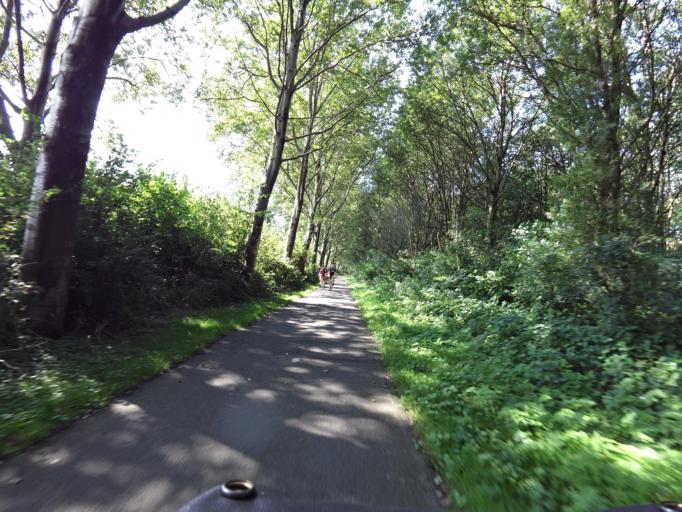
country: NL
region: South Holland
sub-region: Gemeente Barendrecht
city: Barendrecht
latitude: 51.8262
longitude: 4.5154
